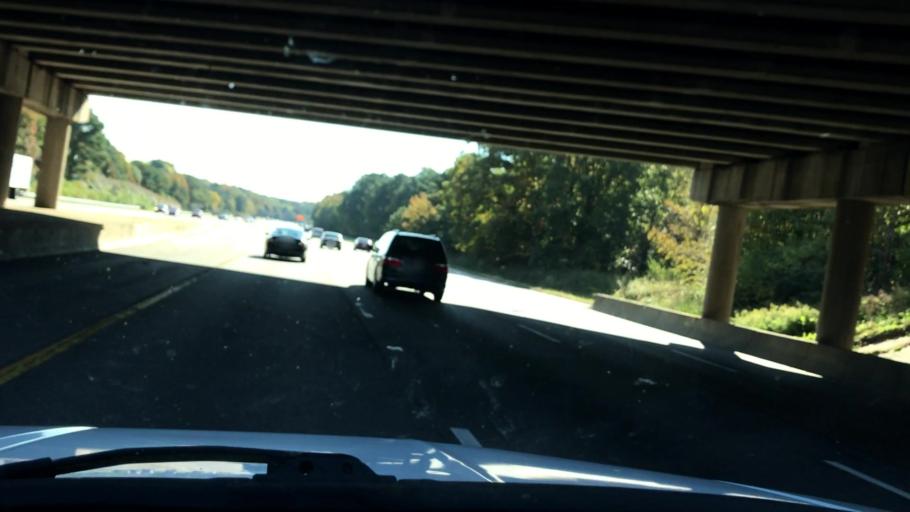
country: US
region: Virginia
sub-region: Henrico County
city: Tuckahoe
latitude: 37.6260
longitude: -77.5549
